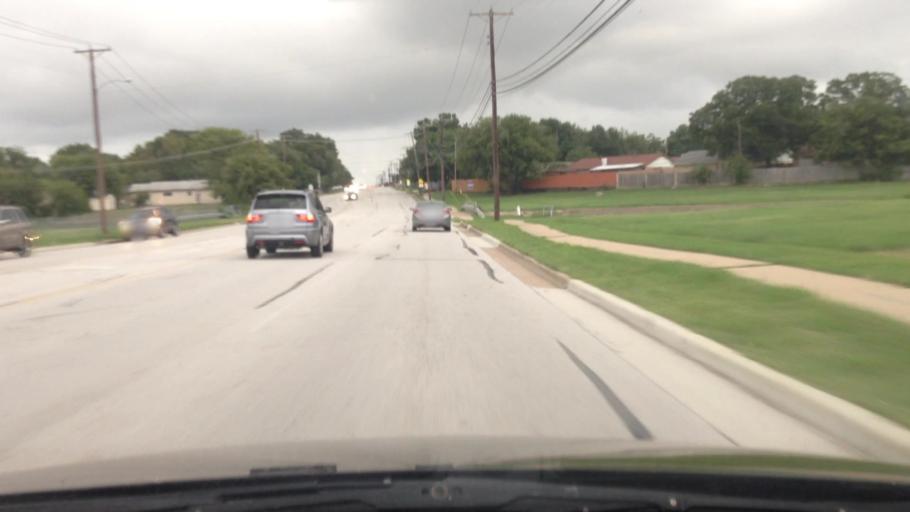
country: US
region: Texas
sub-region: Tarrant County
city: Watauga
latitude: 32.8604
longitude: -97.2484
